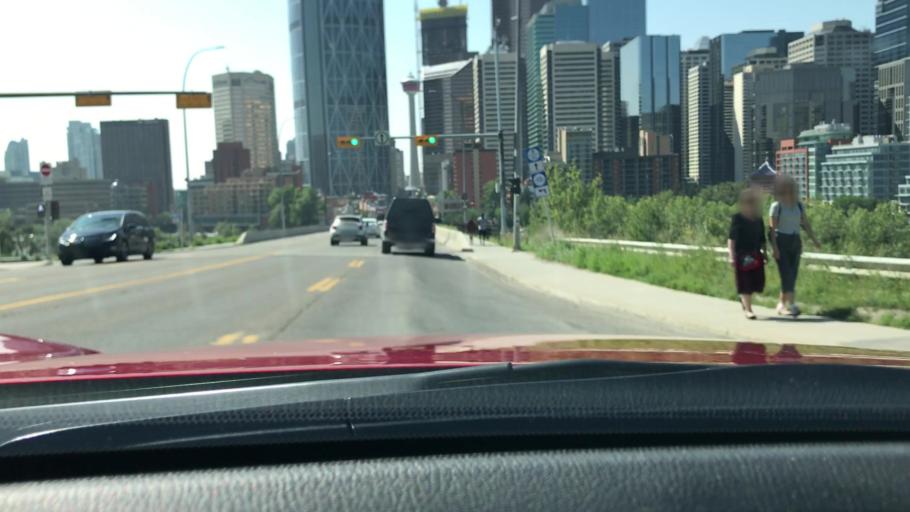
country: CA
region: Alberta
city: Calgary
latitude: 51.0556
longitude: -114.0625
